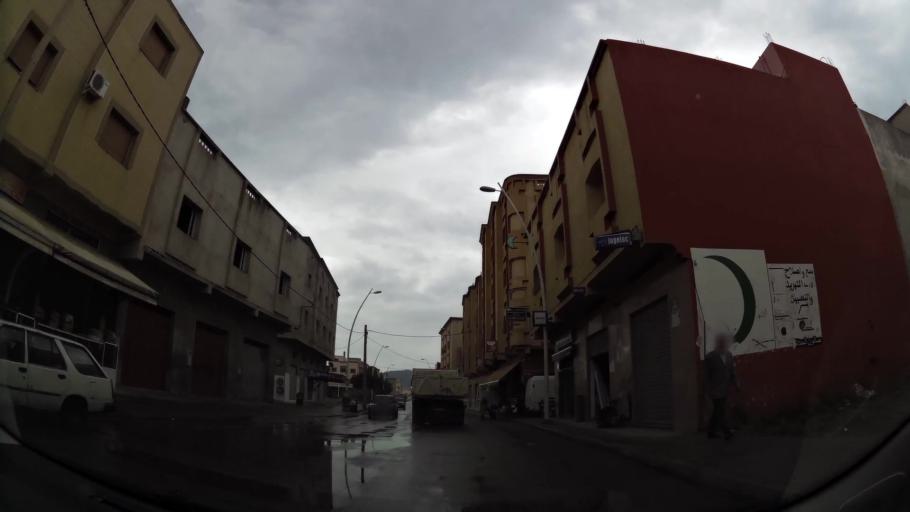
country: MA
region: Oriental
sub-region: Nador
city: Nador
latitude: 35.1522
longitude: -2.9801
